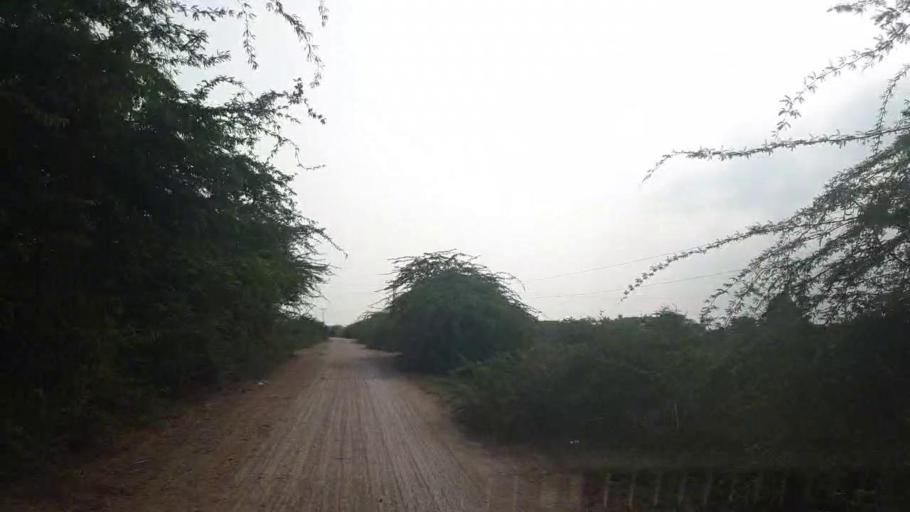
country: PK
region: Sindh
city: Badin
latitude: 24.6229
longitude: 68.6888
